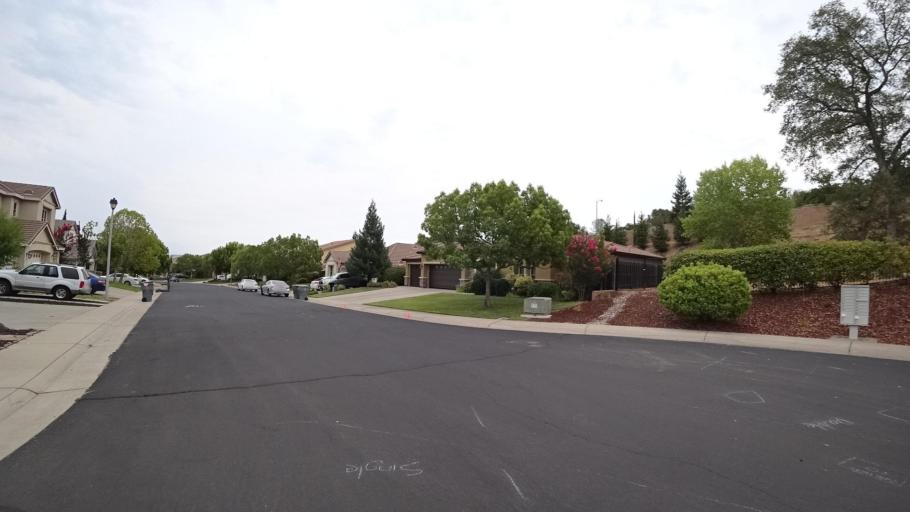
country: US
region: California
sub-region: Placer County
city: Rocklin
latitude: 38.7773
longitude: -121.2037
